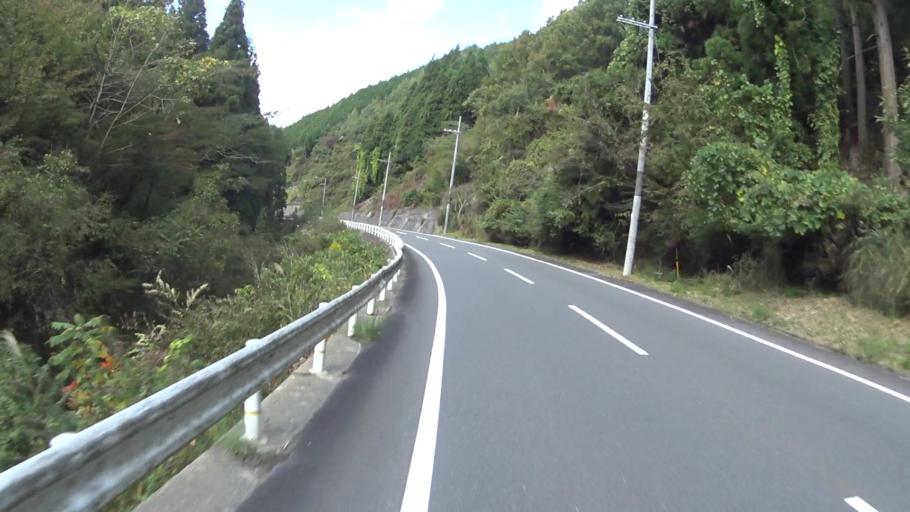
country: JP
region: Kyoto
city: Kameoka
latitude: 35.1202
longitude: 135.5635
